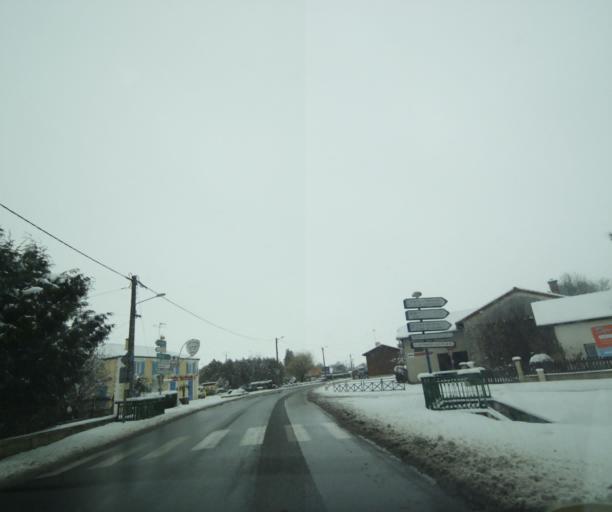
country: FR
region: Champagne-Ardenne
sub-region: Departement de la Haute-Marne
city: Montier-en-Der
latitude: 48.5343
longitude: 4.8173
